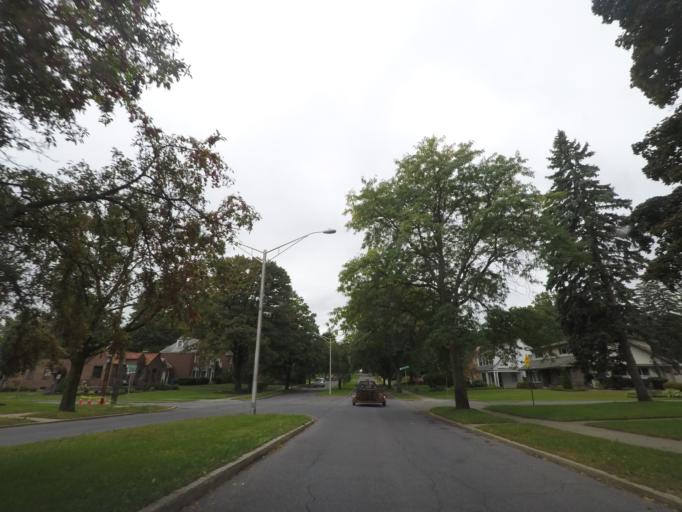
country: US
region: New York
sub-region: Albany County
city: West Albany
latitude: 42.6666
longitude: -73.7964
